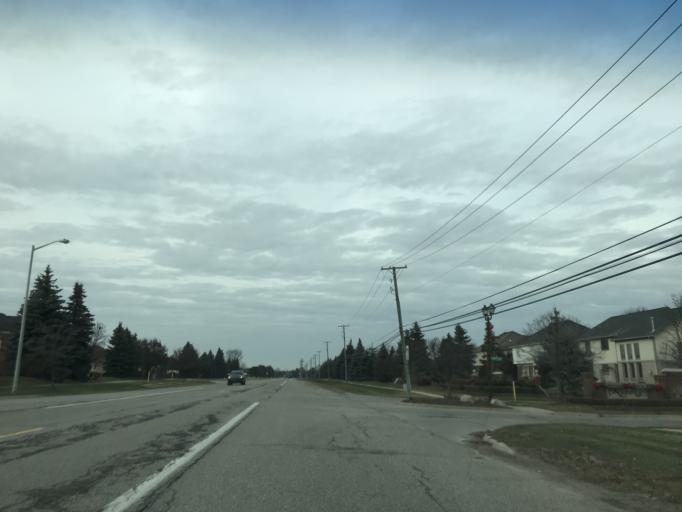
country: US
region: Michigan
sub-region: Macomb County
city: Shelby
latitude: 42.7007
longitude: -82.9643
